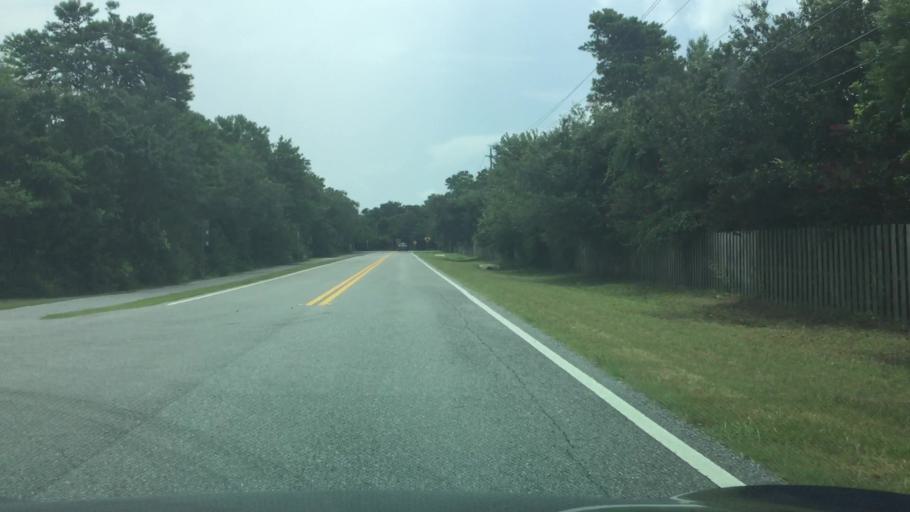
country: US
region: Florida
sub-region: Bay County
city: Upper Grand Lagoon
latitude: 30.1460
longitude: -85.7148
